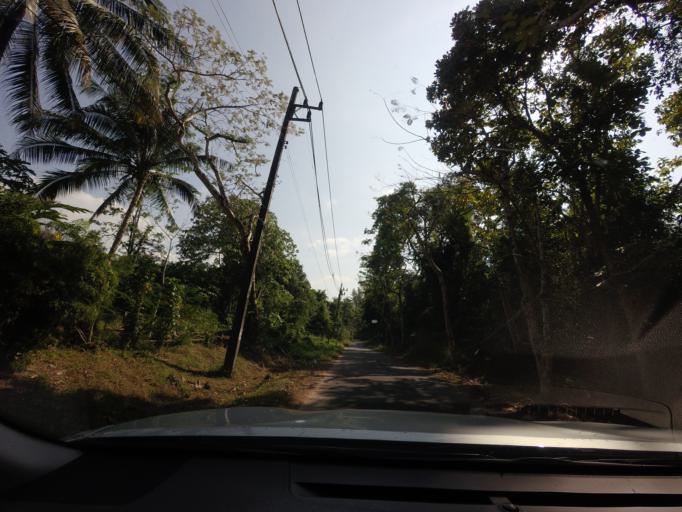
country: TH
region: Phangnga
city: Ban Khao Lak
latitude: 8.7407
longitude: 98.2470
